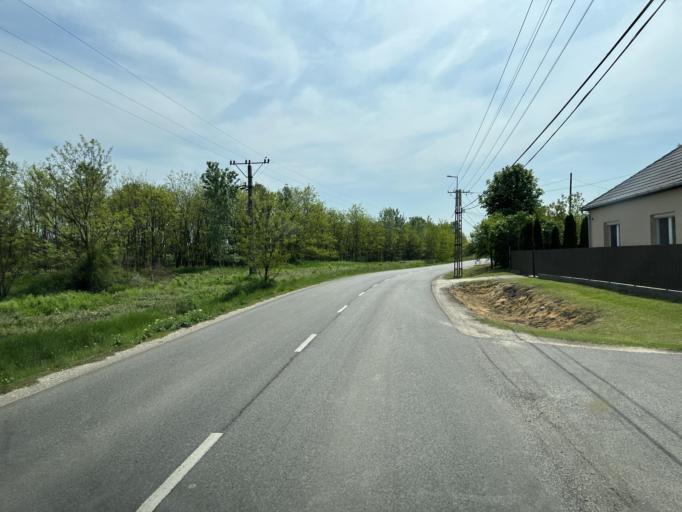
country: HU
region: Pest
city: Abony
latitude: 47.2036
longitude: 20.0109
